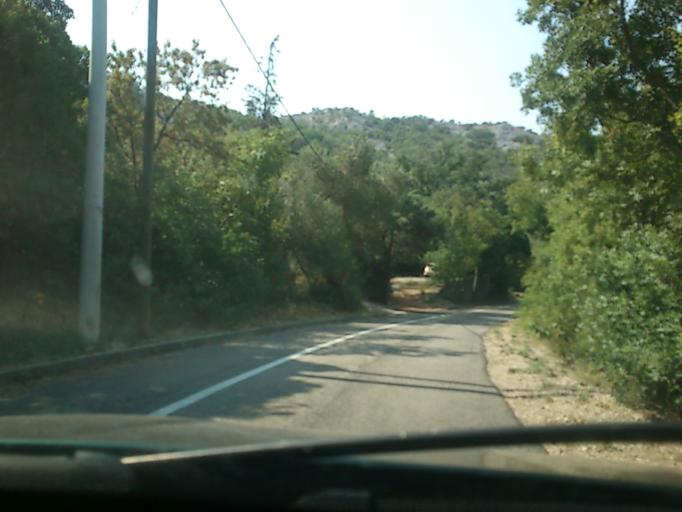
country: HR
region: Primorsko-Goranska
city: Banjol
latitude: 44.7057
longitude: 14.9024
